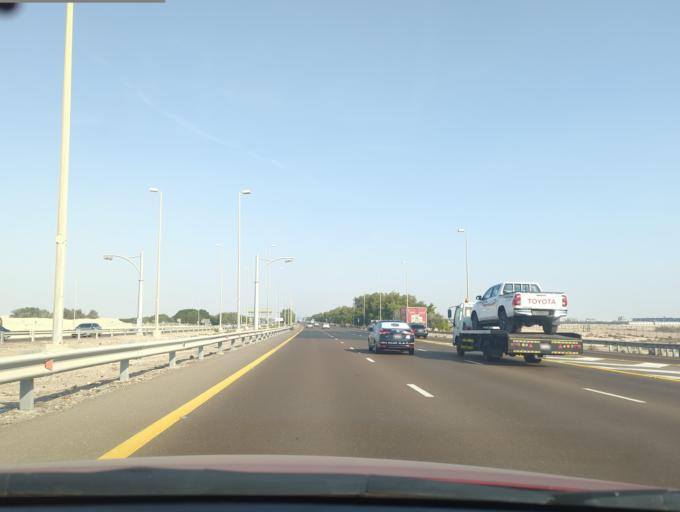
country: AE
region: Abu Dhabi
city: Abu Dhabi
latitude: 24.4097
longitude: 54.6789
